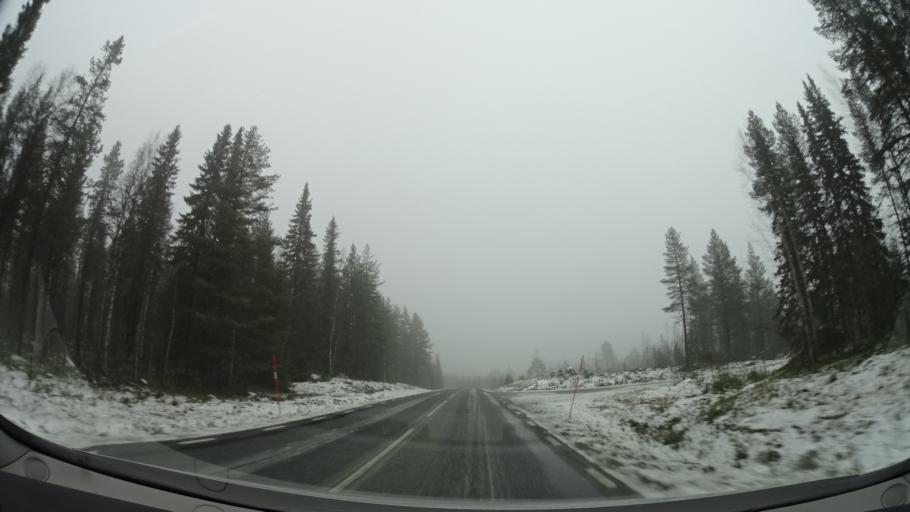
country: SE
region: Vaesterbotten
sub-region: Asele Kommun
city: Insjon
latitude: 64.3465
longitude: 17.8887
